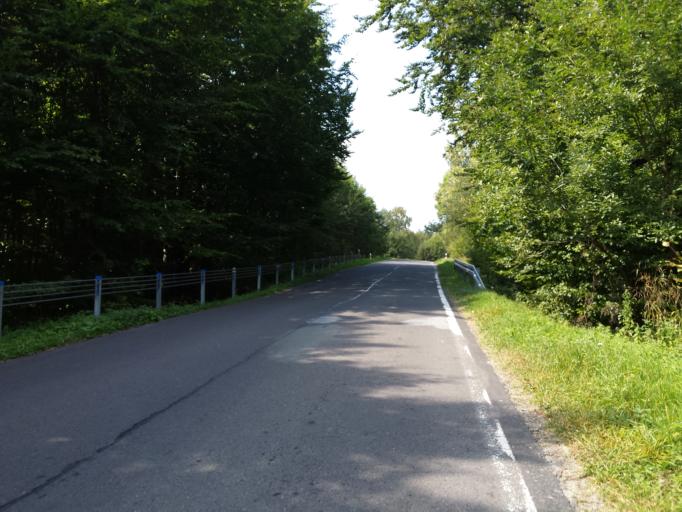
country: PL
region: Subcarpathian Voivodeship
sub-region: Powiat bieszczadzki
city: Lutowiska
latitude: 49.1216
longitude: 22.6031
